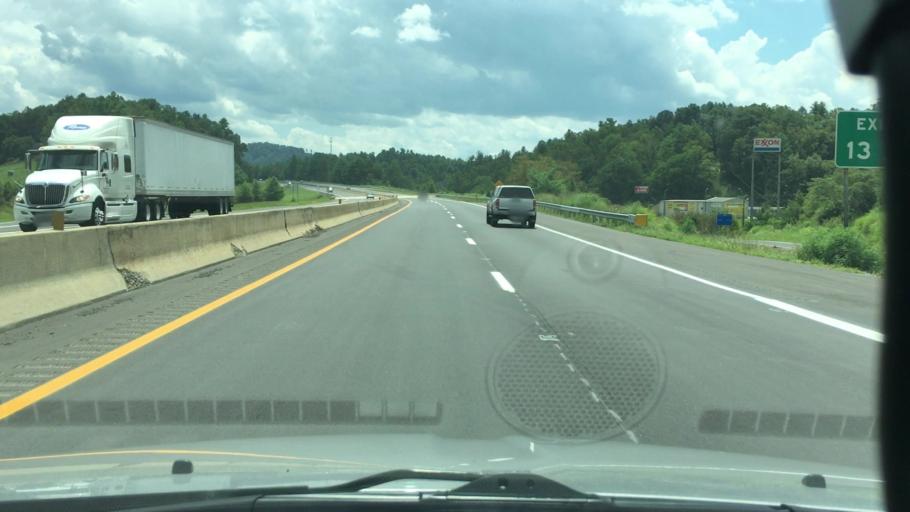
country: US
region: North Carolina
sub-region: Madison County
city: Mars Hill
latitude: 35.7859
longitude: -82.5398
